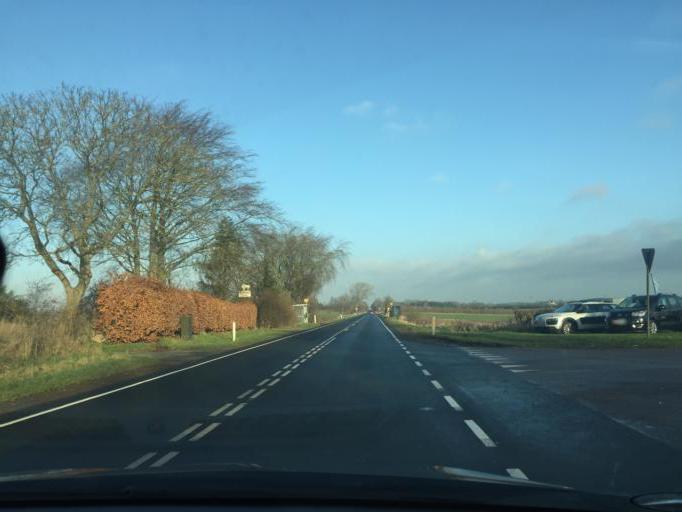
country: DK
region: South Denmark
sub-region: Faaborg-Midtfyn Kommune
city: Faaborg
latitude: 55.1820
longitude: 10.3000
